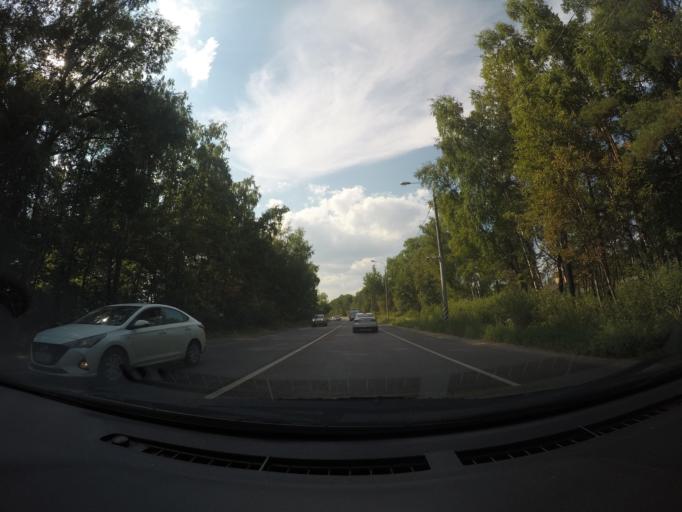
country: RU
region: Moskovskaya
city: Il'inskiy
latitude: 55.6513
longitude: 38.1258
